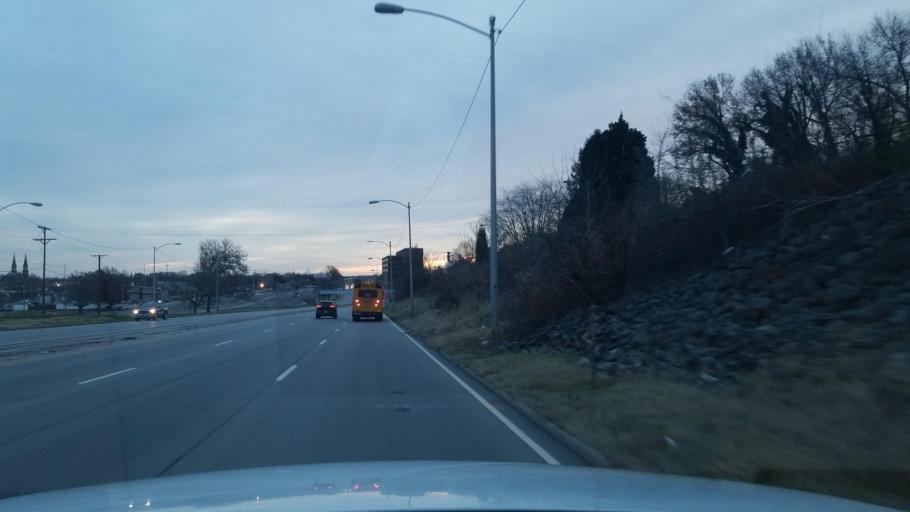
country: US
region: Indiana
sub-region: Vanderburgh County
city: Evansville
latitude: 37.9781
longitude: -87.6065
